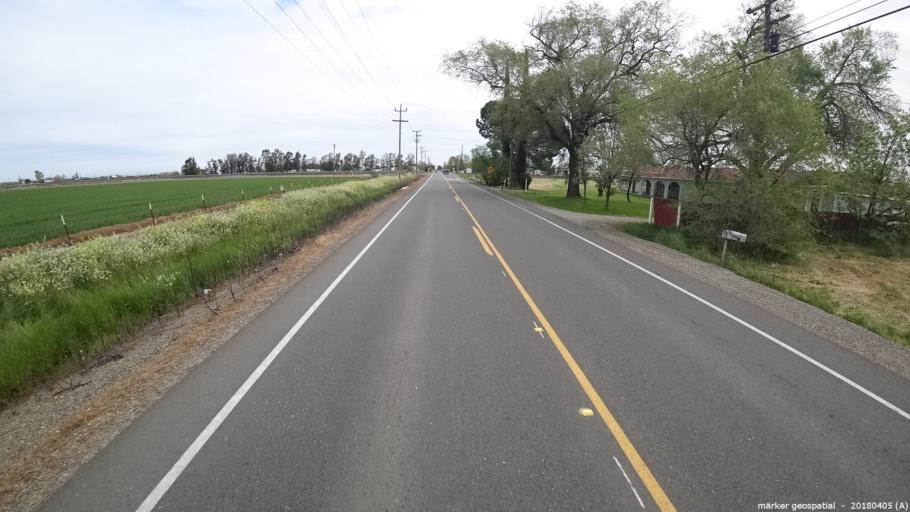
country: US
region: California
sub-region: Sacramento County
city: Galt
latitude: 38.2910
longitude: -121.3226
